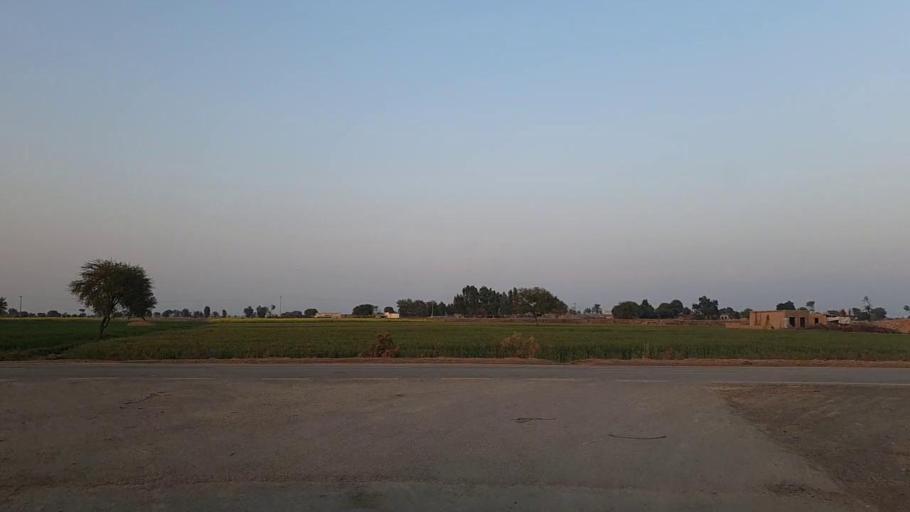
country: PK
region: Sindh
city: Jam Sahib
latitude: 26.3118
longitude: 68.5836
